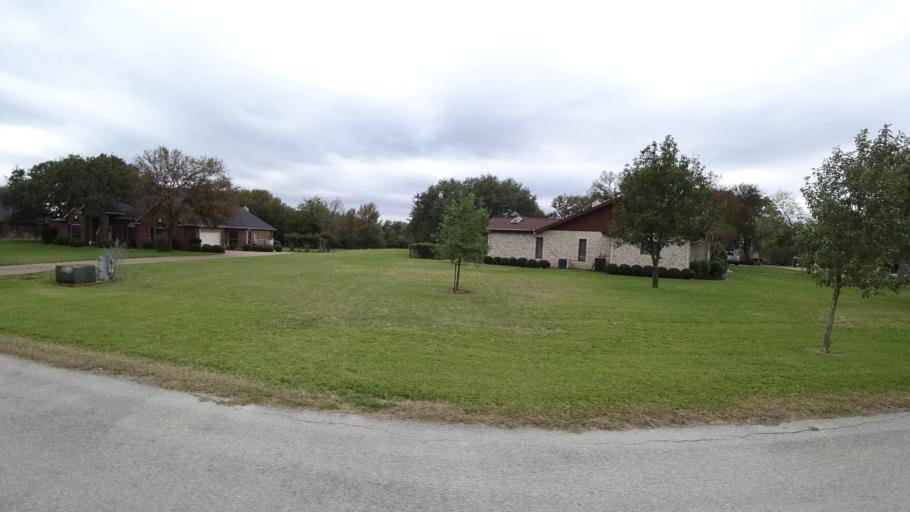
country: US
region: Texas
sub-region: Travis County
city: Shady Hollow
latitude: 30.1537
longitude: -97.8681
